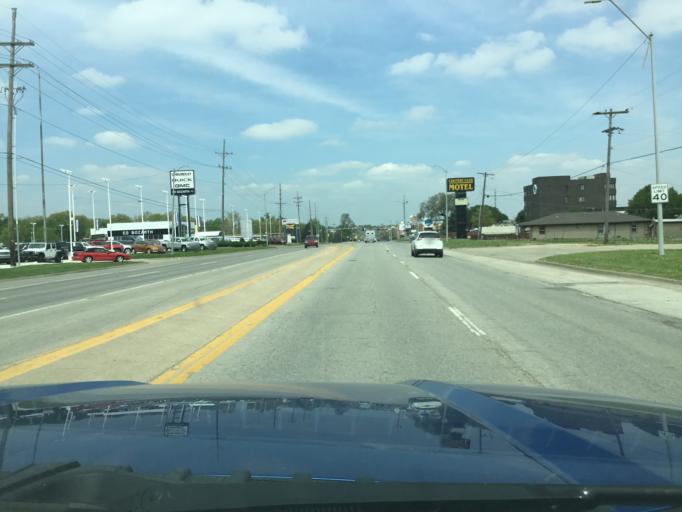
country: US
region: Kansas
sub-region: Shawnee County
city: Topeka
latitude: 38.9980
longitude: -95.6876
